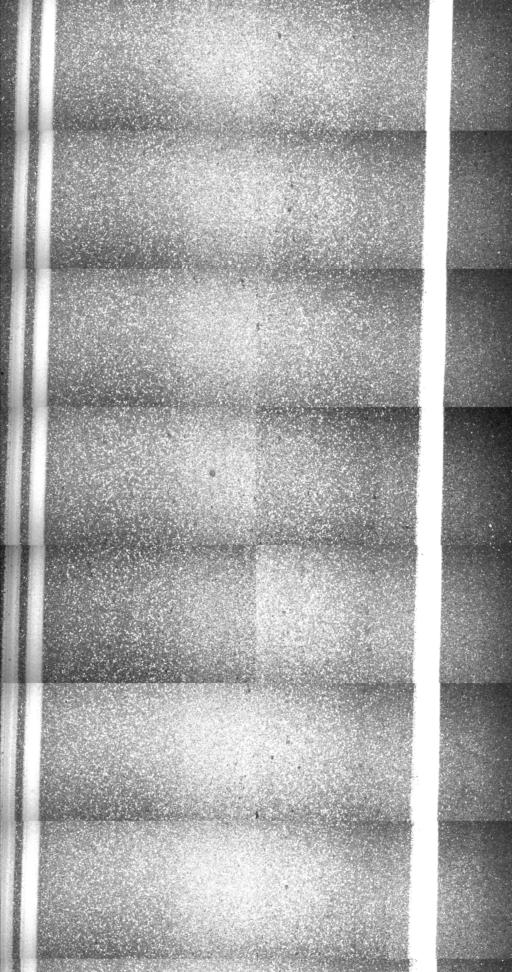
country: US
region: Vermont
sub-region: Orange County
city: Randolph
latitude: 43.7787
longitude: -72.7978
